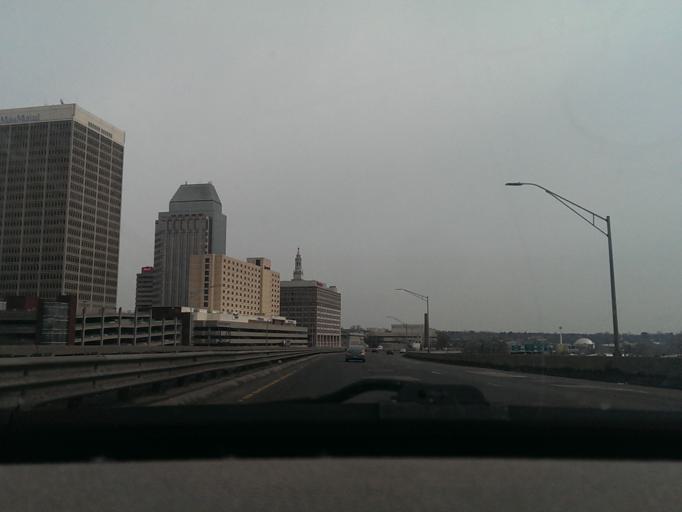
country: US
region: Massachusetts
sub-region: Hampden County
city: Springfield
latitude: 42.1031
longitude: -72.5960
